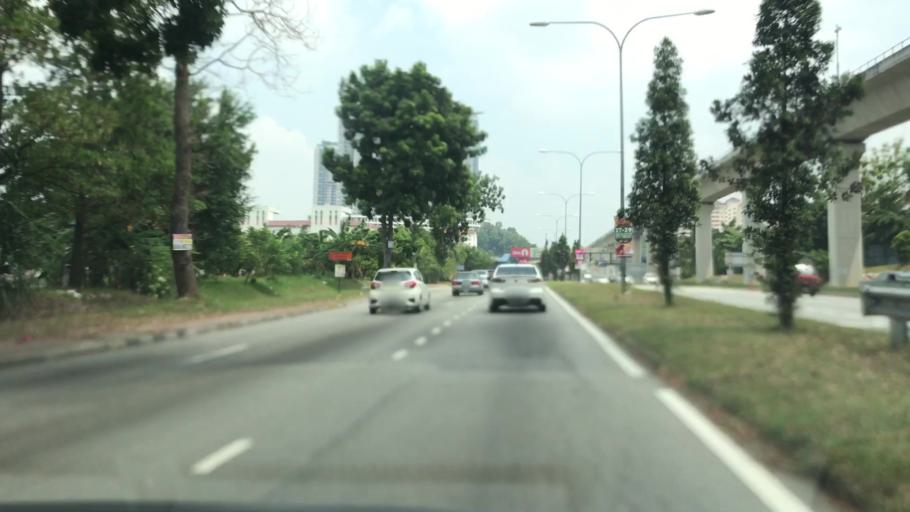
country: MY
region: Selangor
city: Subang Jaya
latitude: 3.0492
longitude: 101.6392
